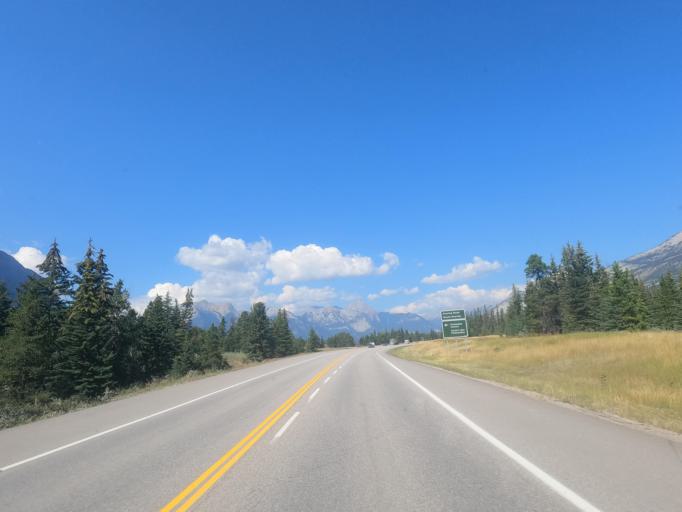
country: CA
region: Alberta
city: Jasper Park Lodge
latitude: 52.9685
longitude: -118.0560
